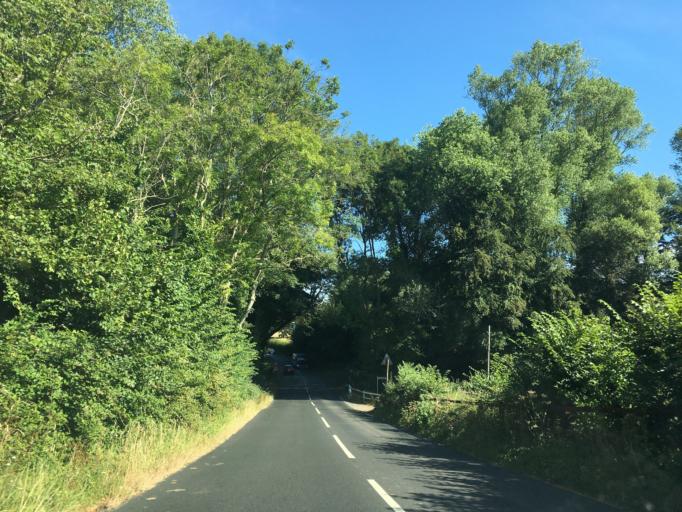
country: GB
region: England
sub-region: Isle of Wight
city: Newport
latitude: 50.6640
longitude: -1.2990
